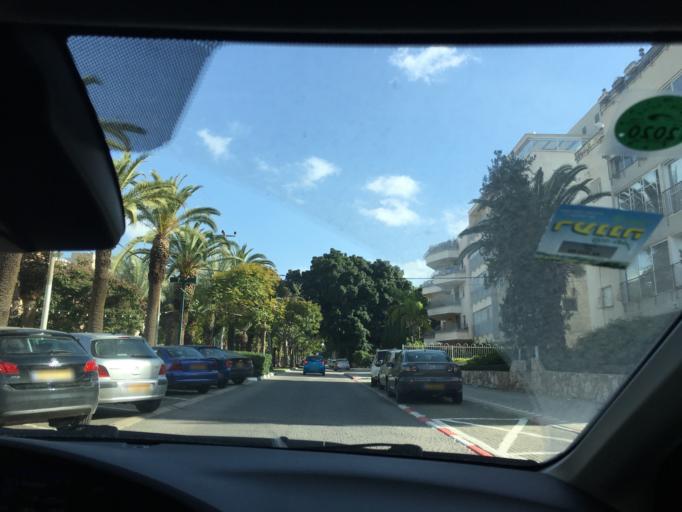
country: IL
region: Tel Aviv
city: Ramat HaSharon
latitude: 32.1452
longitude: 34.8408
